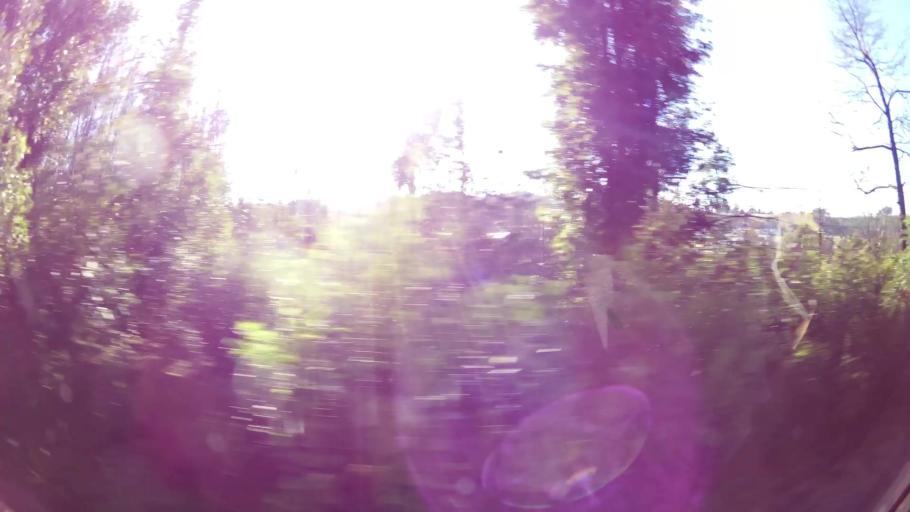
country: ZA
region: Western Cape
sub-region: Eden District Municipality
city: Knysna
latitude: -34.0251
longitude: 23.0085
